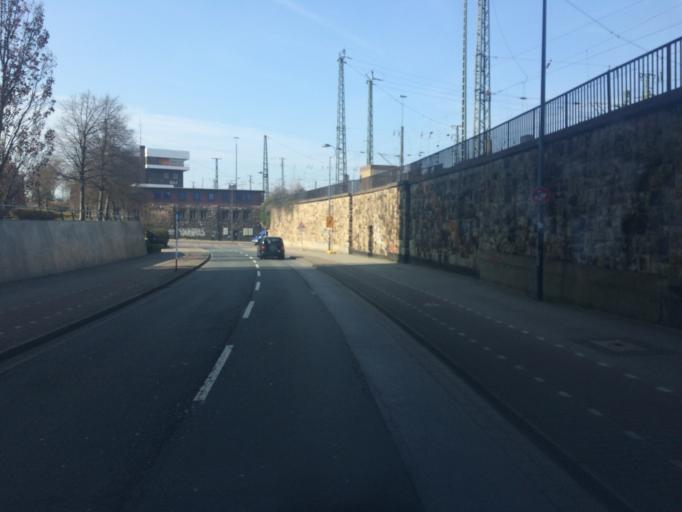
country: DE
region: North Rhine-Westphalia
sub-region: Regierungsbezirk Arnsberg
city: Dortmund
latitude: 51.5166
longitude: 7.4554
